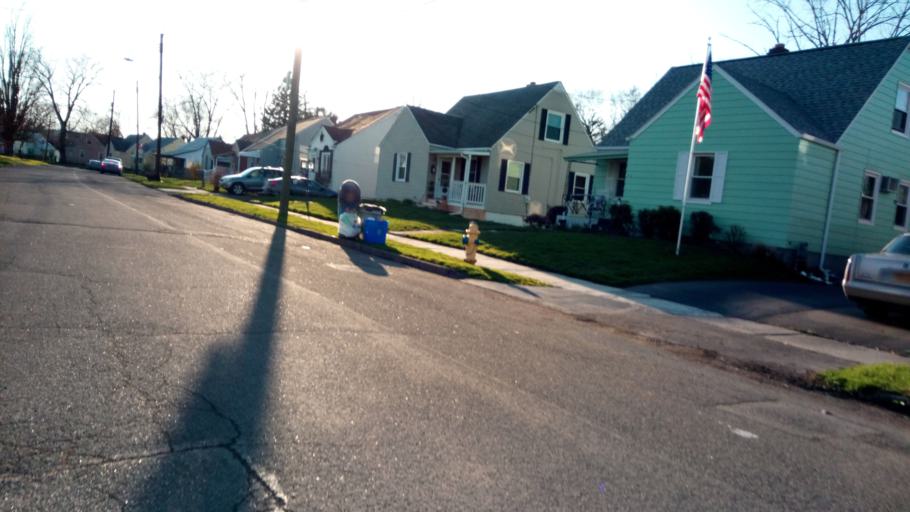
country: US
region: New York
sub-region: Chemung County
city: Elmira
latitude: 42.0804
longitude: -76.7840
